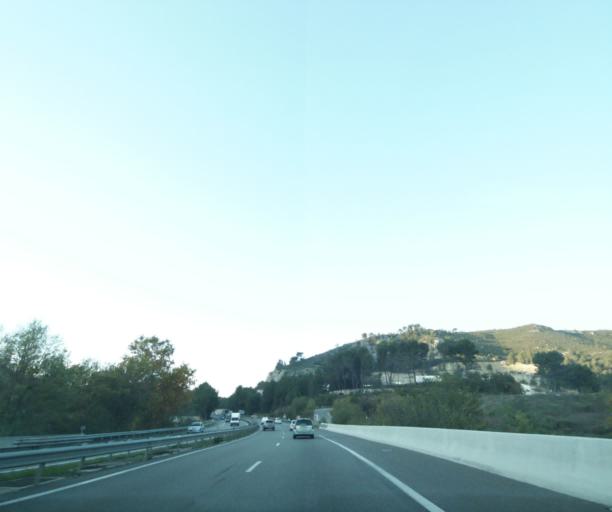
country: FR
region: Provence-Alpes-Cote d'Azur
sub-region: Departement des Bouches-du-Rhone
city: La Destrousse
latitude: 43.3650
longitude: 5.6135
